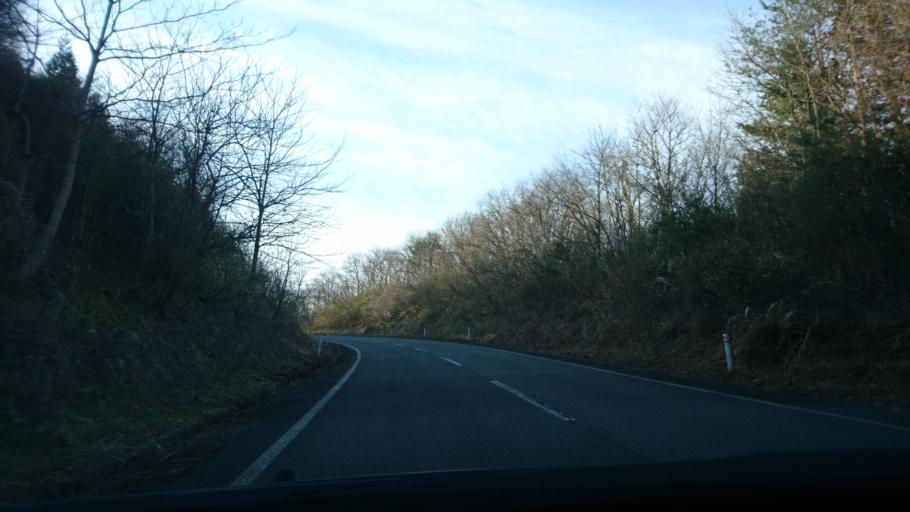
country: JP
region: Iwate
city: Ichinoseki
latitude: 38.8601
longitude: 141.1990
